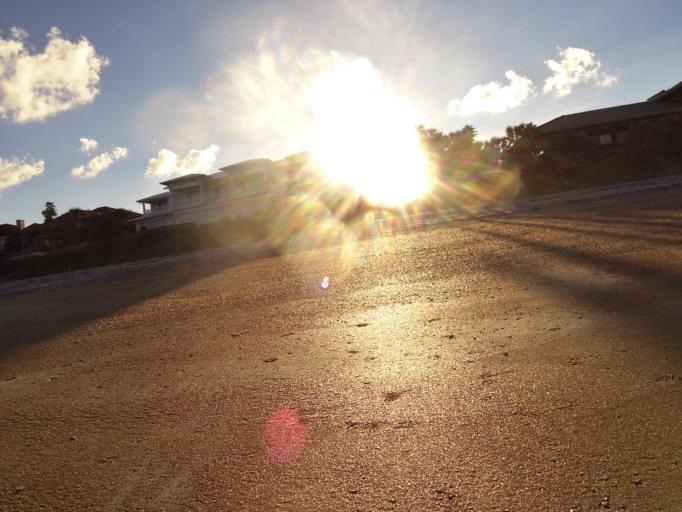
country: US
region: Florida
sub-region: Saint Johns County
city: Sawgrass
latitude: 30.1753
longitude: -81.3591
